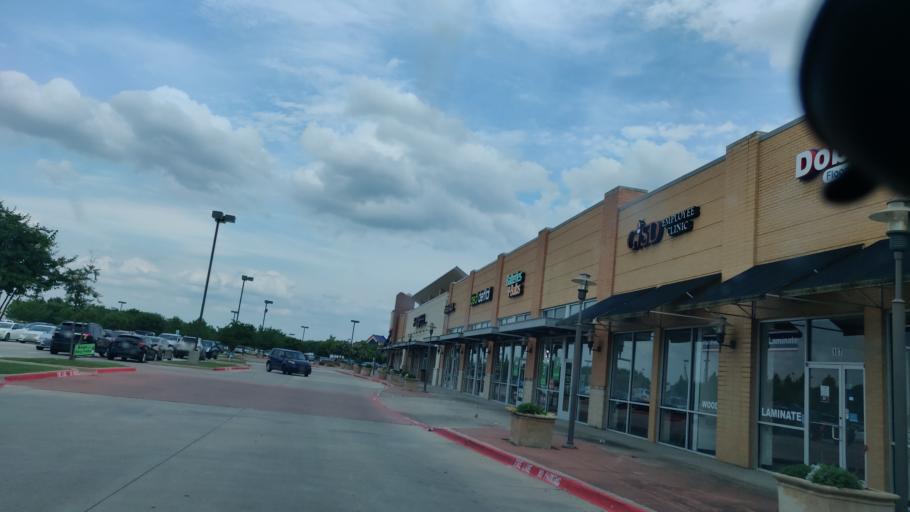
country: US
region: Texas
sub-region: Dallas County
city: Sachse
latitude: 32.9456
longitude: -96.6136
